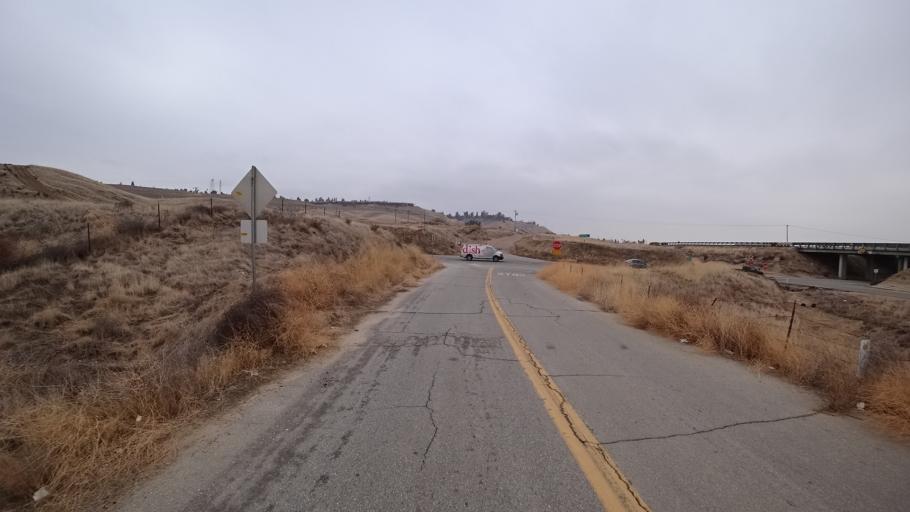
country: US
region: California
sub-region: Kern County
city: Oildale
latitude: 35.4214
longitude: -118.9481
